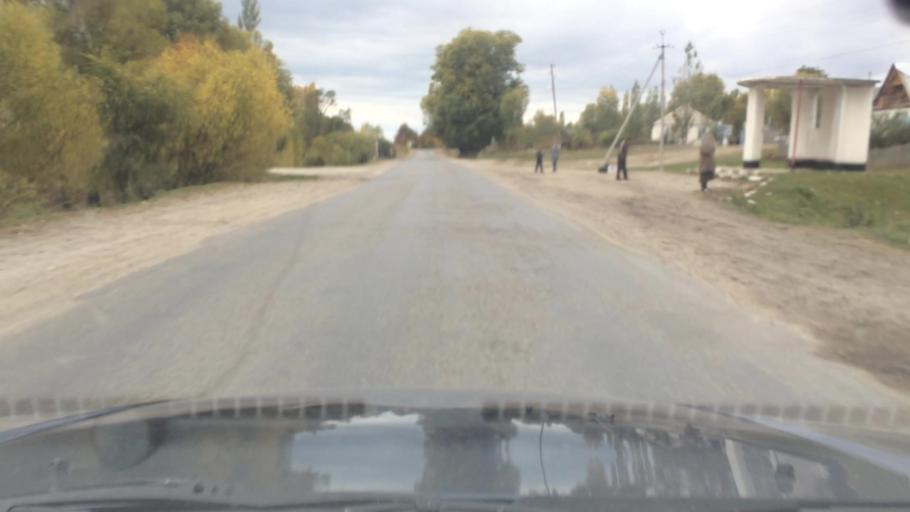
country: KG
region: Ysyk-Koel
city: Tyup
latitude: 42.7679
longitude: 78.1851
